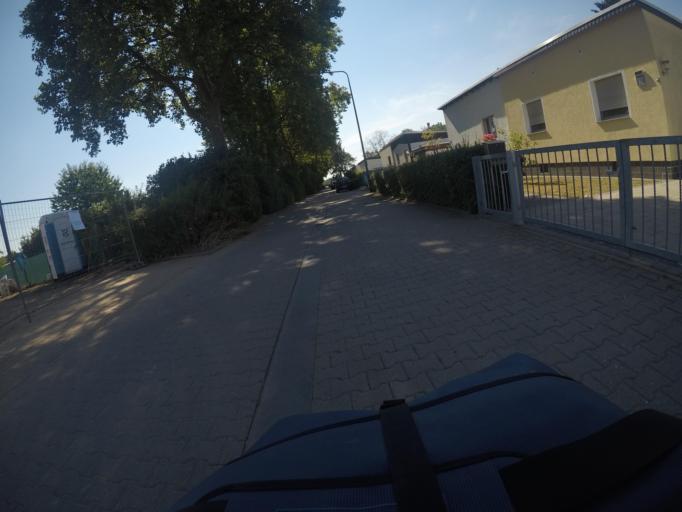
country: DE
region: Hesse
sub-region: Regierungsbezirk Darmstadt
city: Eschborn
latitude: 50.1126
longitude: 8.5971
